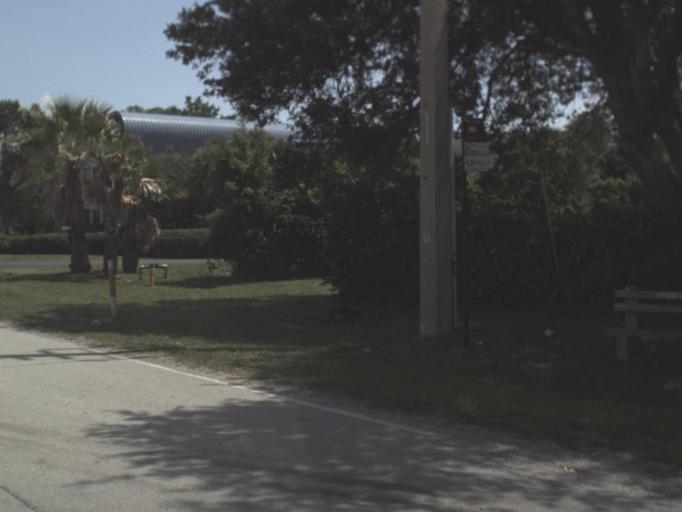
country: US
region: Florida
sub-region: Duval County
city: Jacksonville
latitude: 30.2834
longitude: -81.6307
